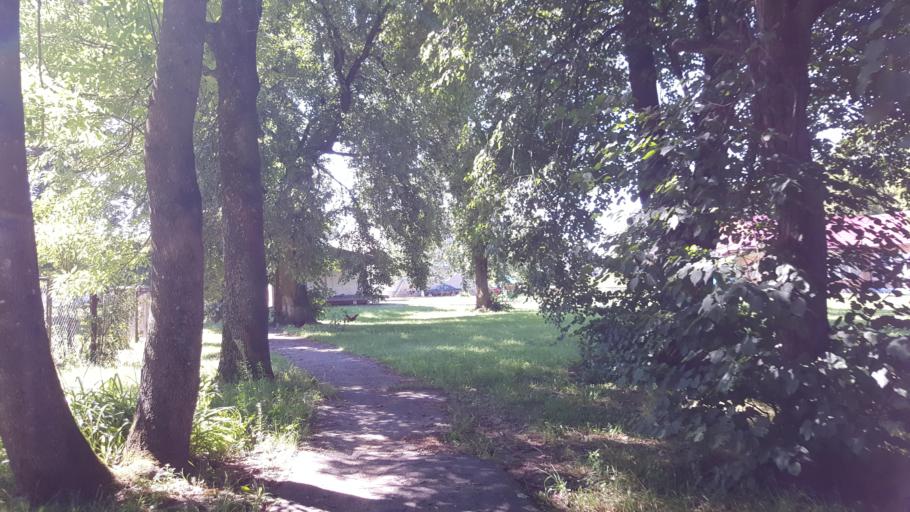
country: BY
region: Brest
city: Kamyanyets
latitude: 52.3846
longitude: 23.6558
